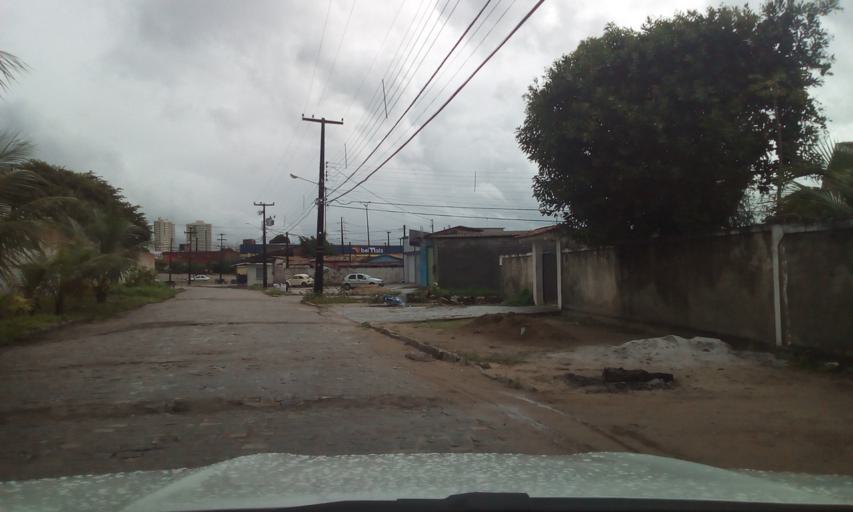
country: BR
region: Paraiba
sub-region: Joao Pessoa
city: Joao Pessoa
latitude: -7.1651
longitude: -34.8483
